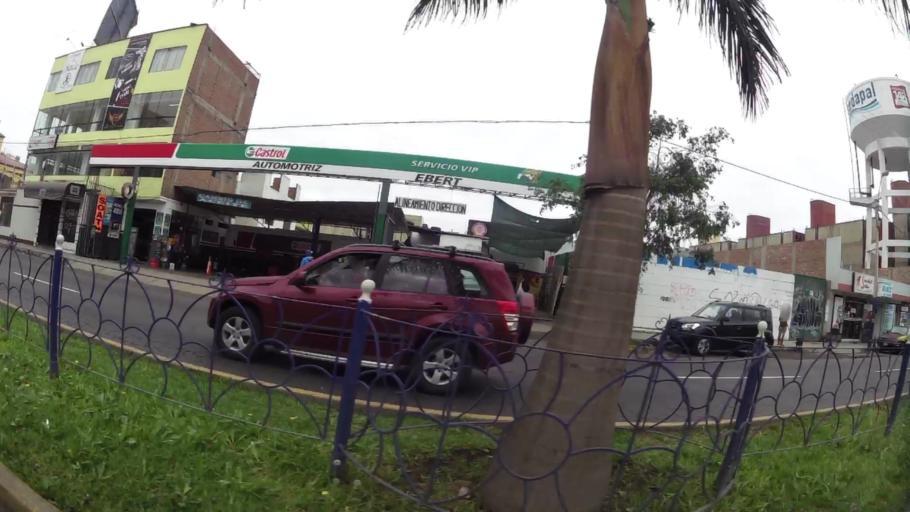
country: PE
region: Lima
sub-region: Lima
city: Surco
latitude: -12.1761
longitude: -76.9990
